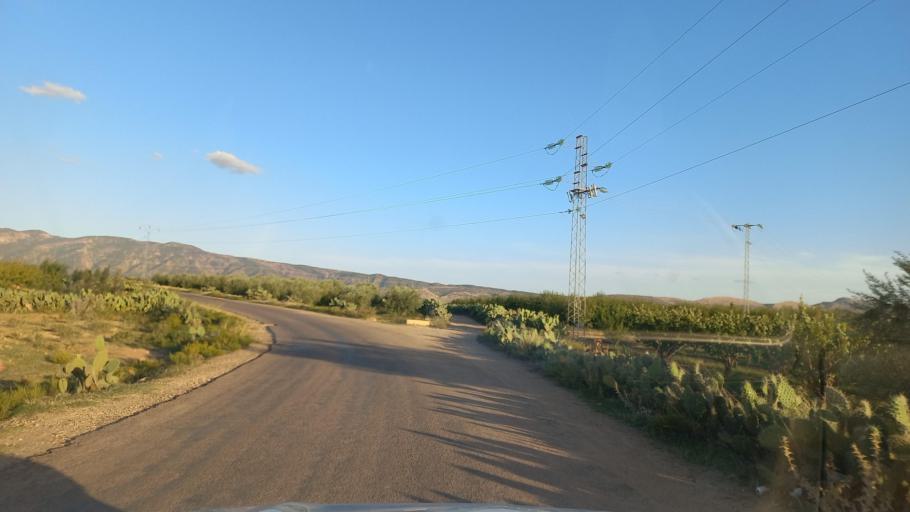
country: TN
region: Al Qasrayn
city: Sbiba
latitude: 35.4257
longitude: 9.1311
